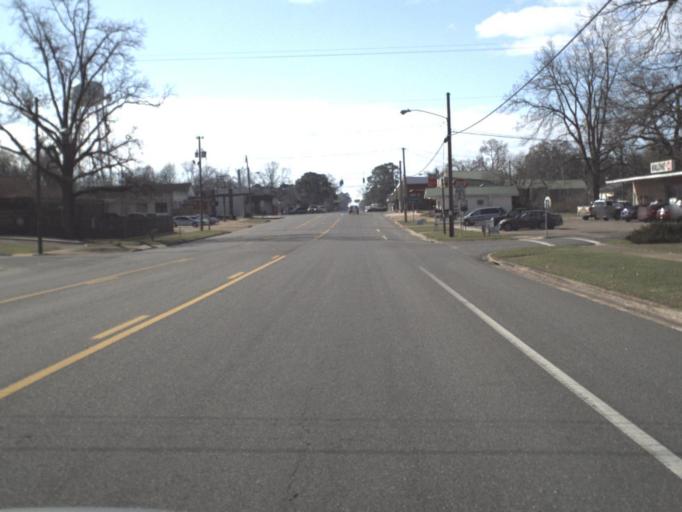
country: US
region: Florida
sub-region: Jackson County
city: Malone
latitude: 30.9594
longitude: -85.1622
